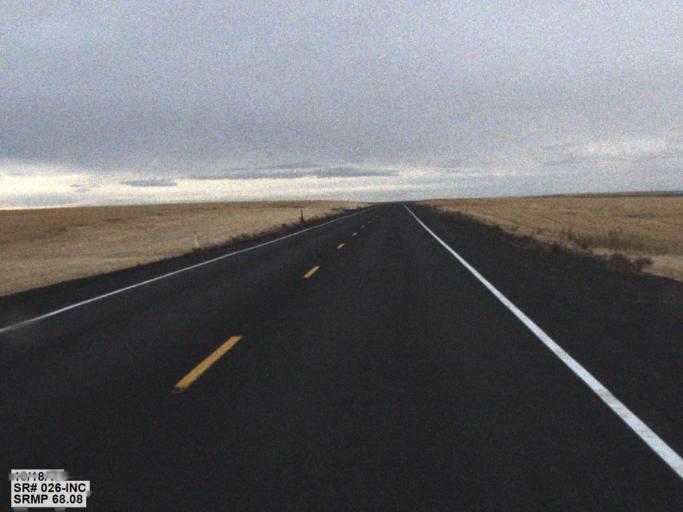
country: US
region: Washington
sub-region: Franklin County
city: Connell
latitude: 46.7945
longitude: -118.6002
